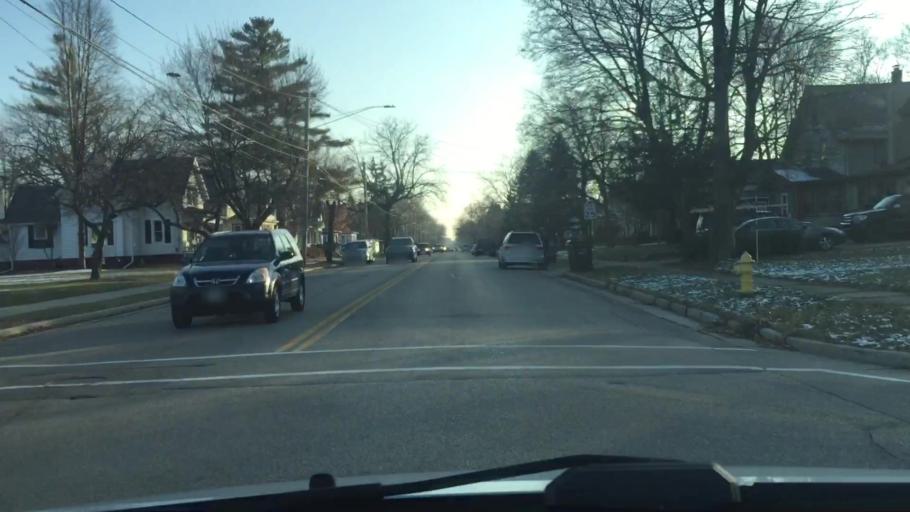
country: US
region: Wisconsin
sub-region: Waukesha County
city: Oconomowoc
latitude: 43.1051
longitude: -88.4959
